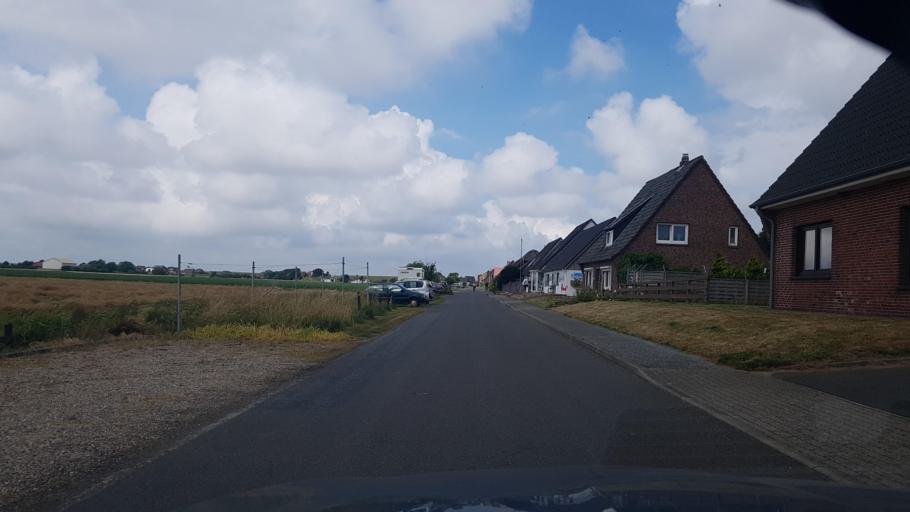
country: DE
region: Schleswig-Holstein
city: Elisabeth-Sophien-Koog
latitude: 54.5039
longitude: 8.8420
